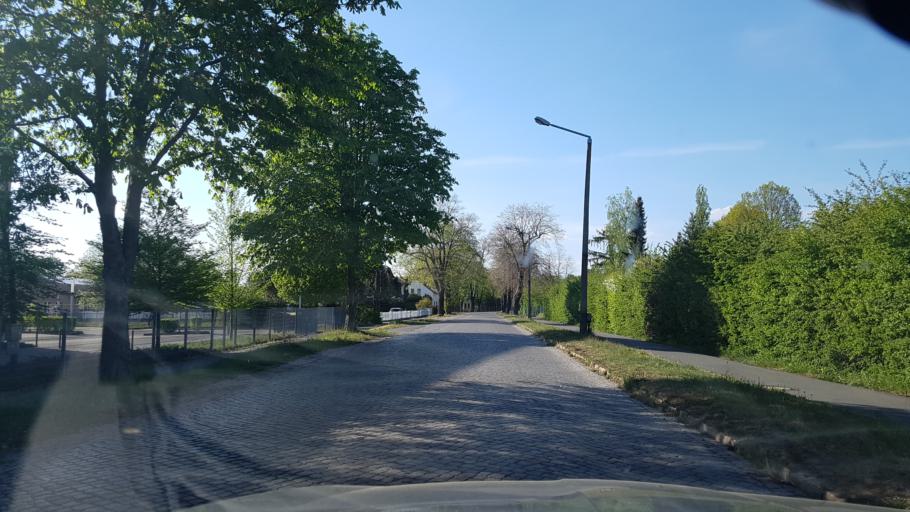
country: DE
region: Brandenburg
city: Elsterwerda
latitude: 51.4661
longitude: 13.5166
